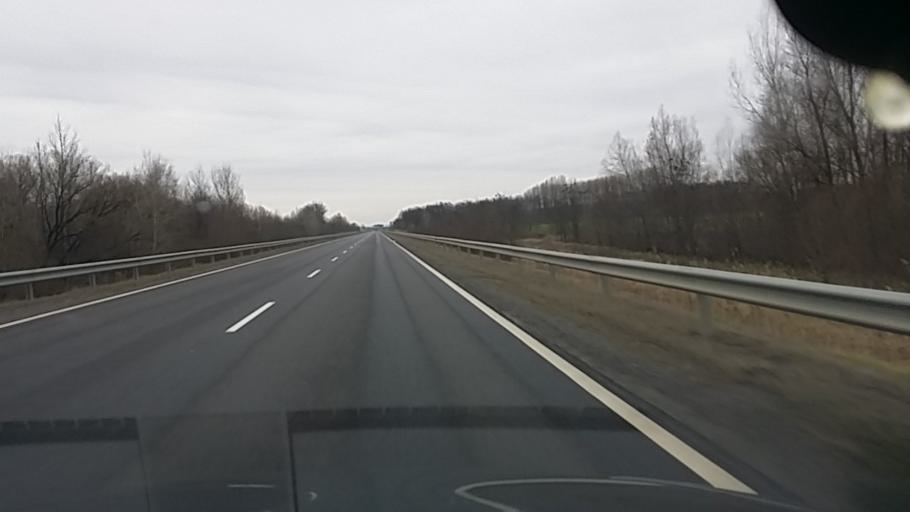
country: HU
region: Szabolcs-Szatmar-Bereg
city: Nagykallo
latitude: 47.9130
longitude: 21.8186
